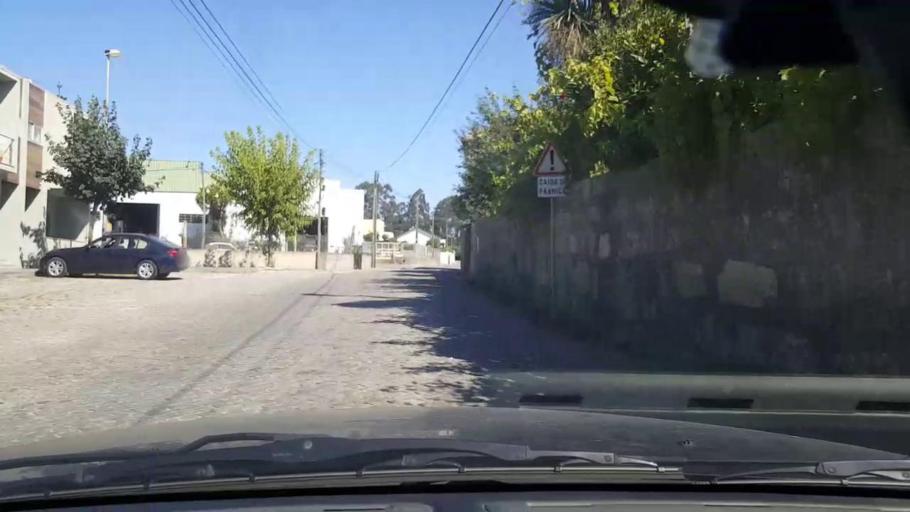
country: PT
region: Porto
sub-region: Maia
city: Gemunde
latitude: 41.2806
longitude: -8.6727
